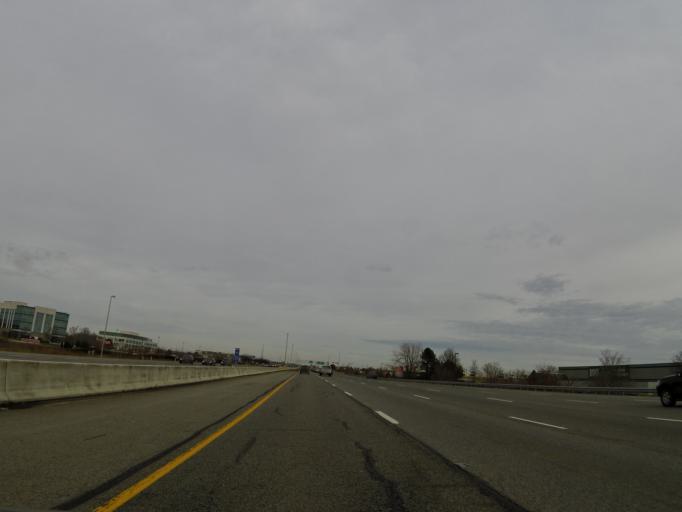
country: US
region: Indiana
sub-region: Marion County
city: Speedway
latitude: 39.8711
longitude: -86.2683
